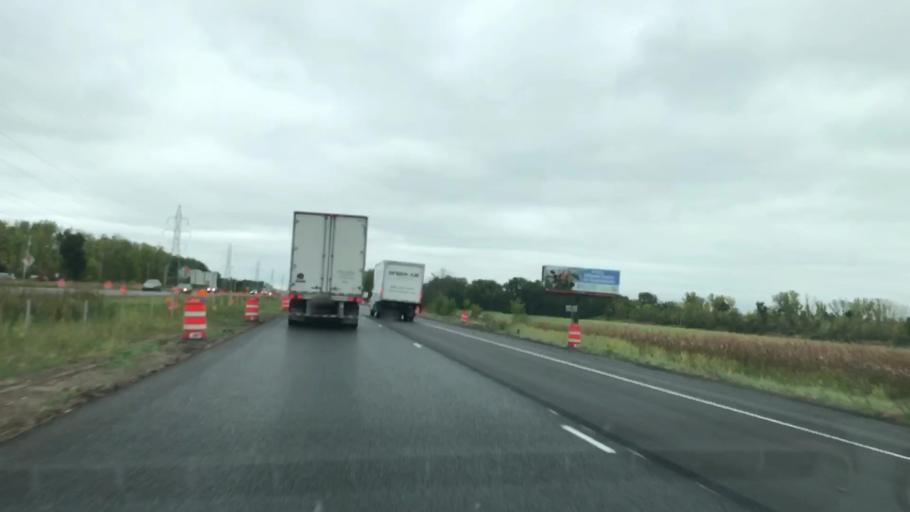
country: US
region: Wisconsin
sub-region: Brown County
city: Suamico
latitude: 44.6191
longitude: -88.0508
